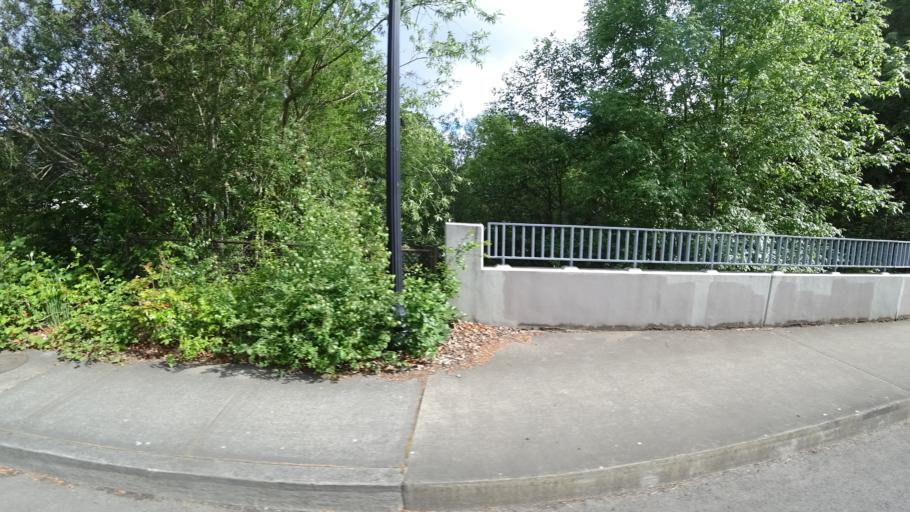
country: US
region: Oregon
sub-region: Washington County
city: Beaverton
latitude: 45.4657
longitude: -122.8341
